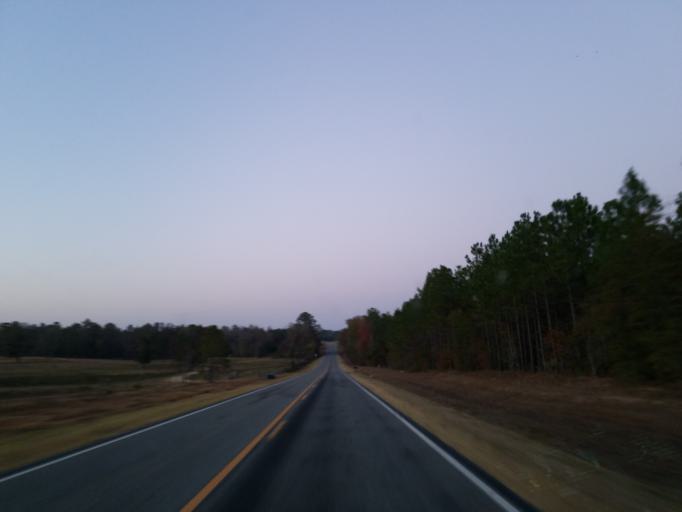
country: US
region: Georgia
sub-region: Wilcox County
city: Rochelle
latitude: 31.8373
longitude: -83.5633
